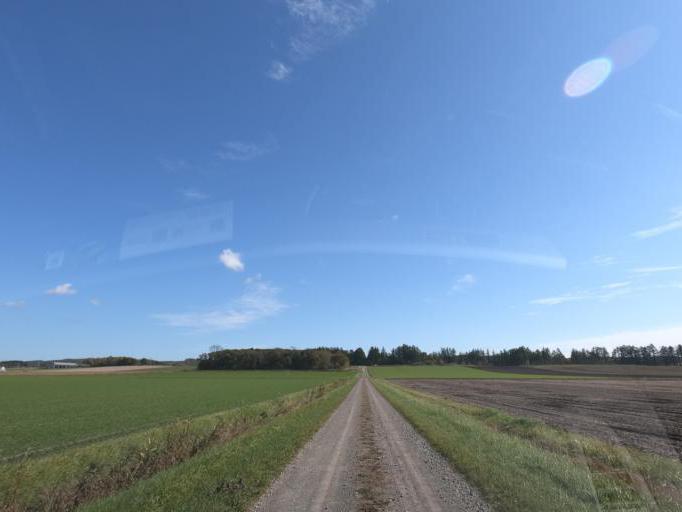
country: JP
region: Hokkaido
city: Otofuke
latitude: 43.0323
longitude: 143.2710
